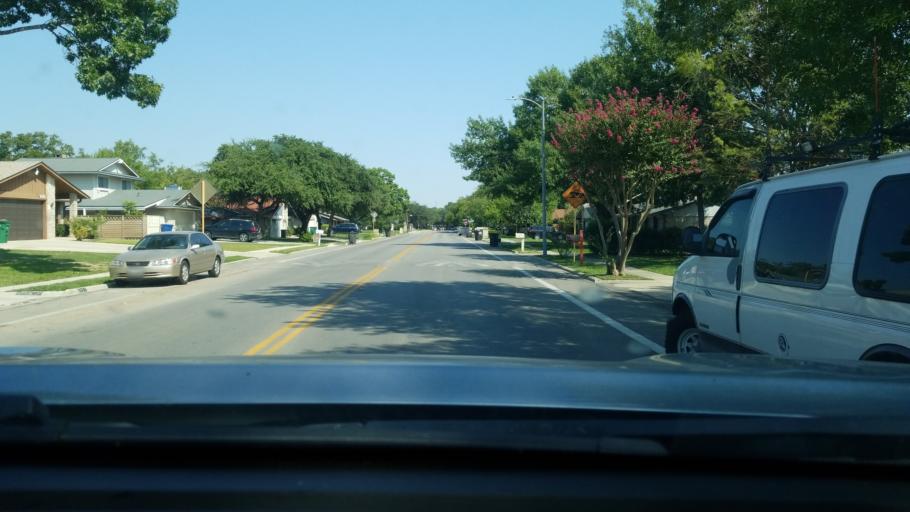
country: US
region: Texas
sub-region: Bexar County
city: Leon Valley
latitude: 29.5544
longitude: -98.6076
